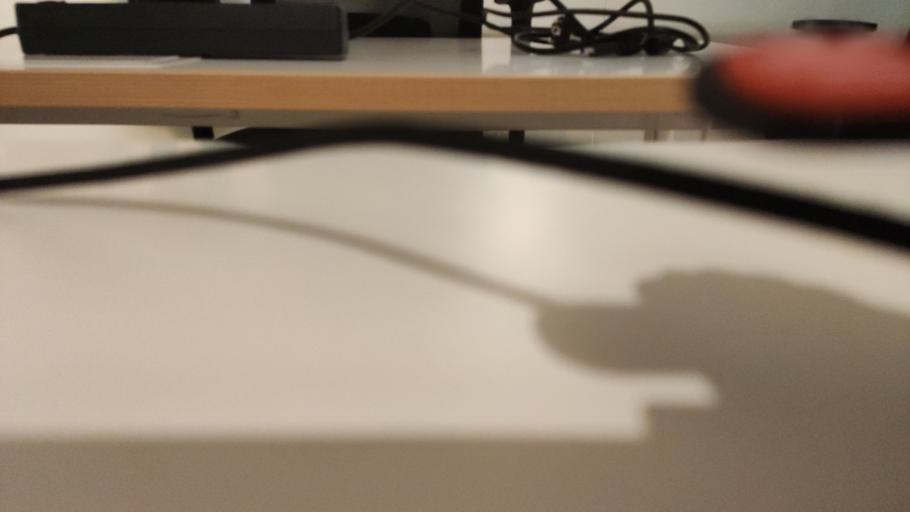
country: RU
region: Moskovskaya
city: Obolensk
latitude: 54.9874
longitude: 37.3104
